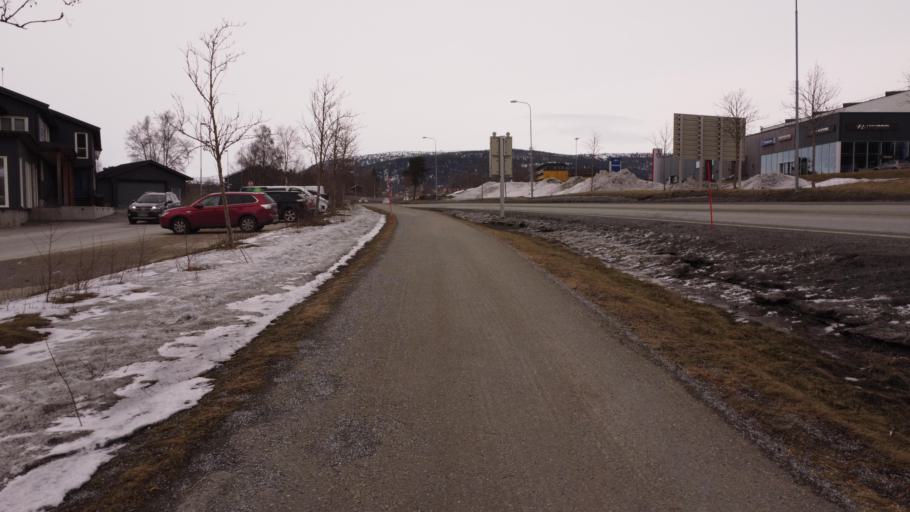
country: NO
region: Nordland
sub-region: Rana
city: Mo i Rana
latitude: 66.3101
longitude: 14.1535
